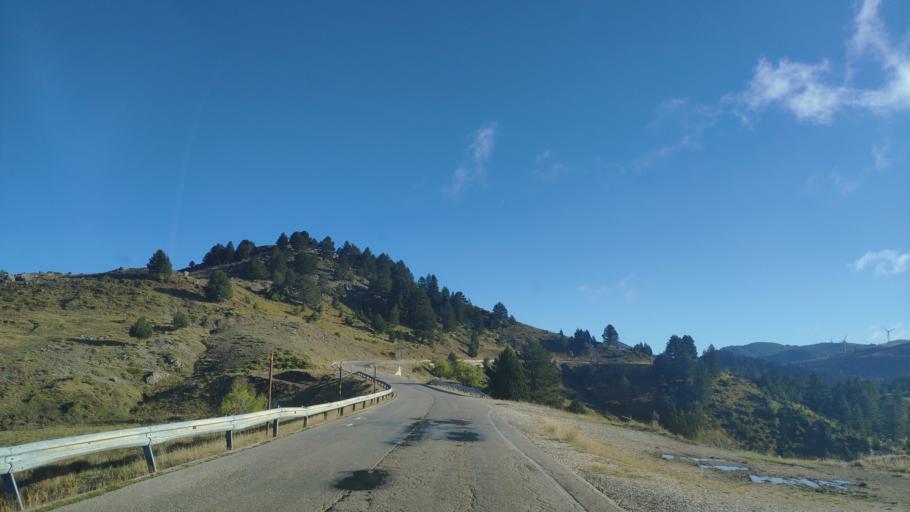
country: GR
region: Epirus
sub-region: Nomos Ioanninon
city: Metsovo
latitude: 39.7953
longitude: 21.1679
